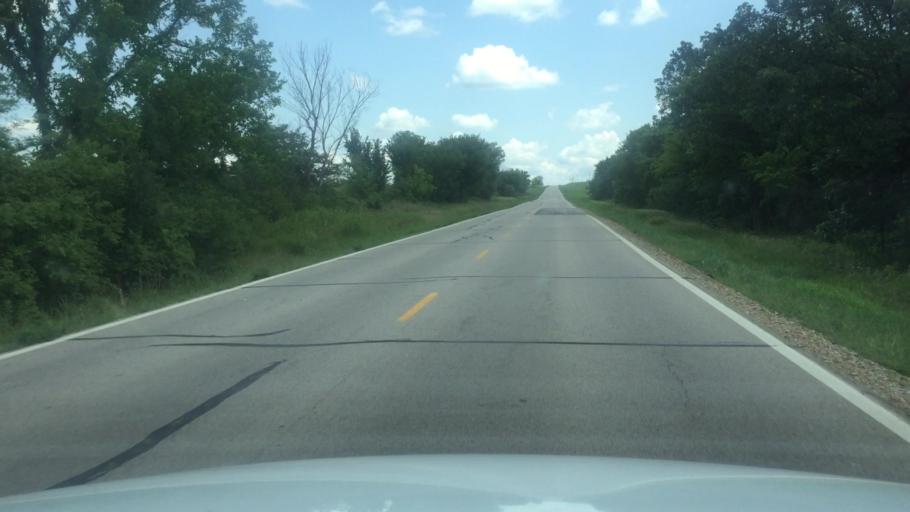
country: US
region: Kansas
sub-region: Brown County
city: Horton
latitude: 39.6674
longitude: -95.6279
